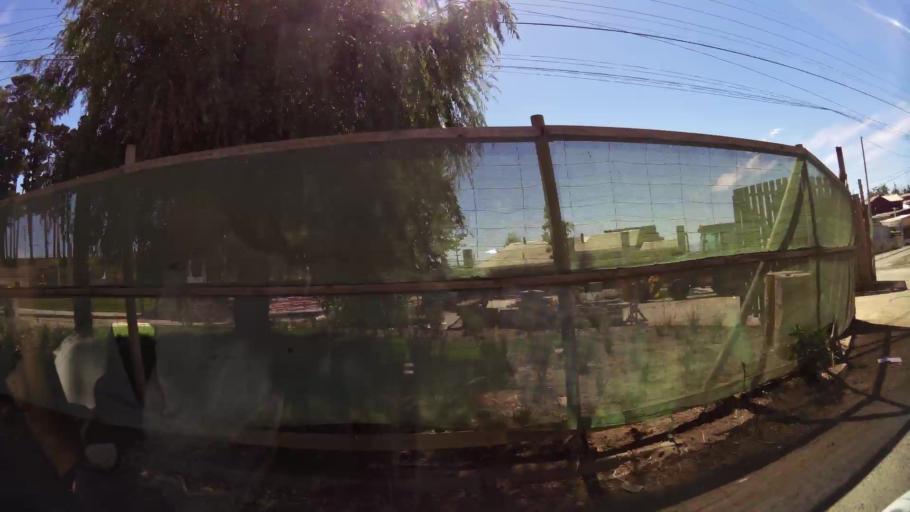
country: CL
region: Biobio
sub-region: Provincia de Concepcion
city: Penco
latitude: -36.7297
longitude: -72.9892
